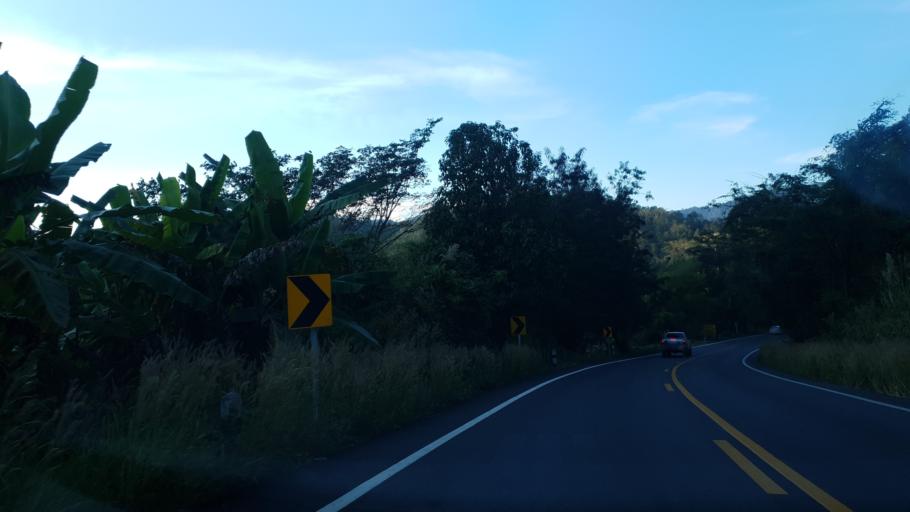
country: TH
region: Loei
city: Dan Sai
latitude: 17.2299
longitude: 101.0564
